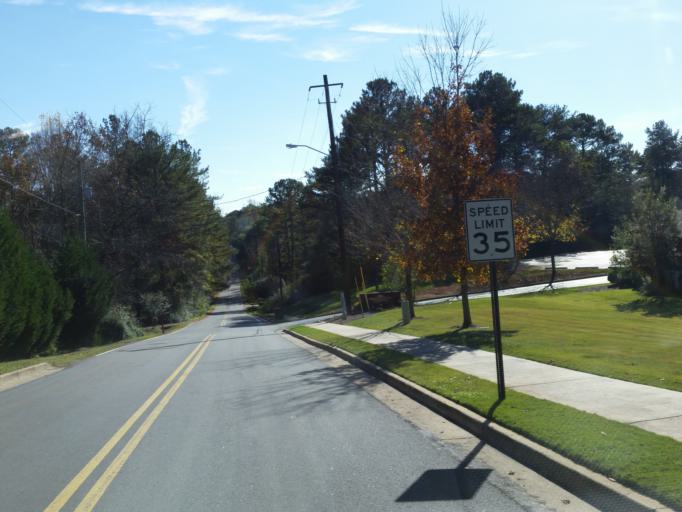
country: US
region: Georgia
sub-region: Cherokee County
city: Woodstock
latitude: 34.0428
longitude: -84.4852
